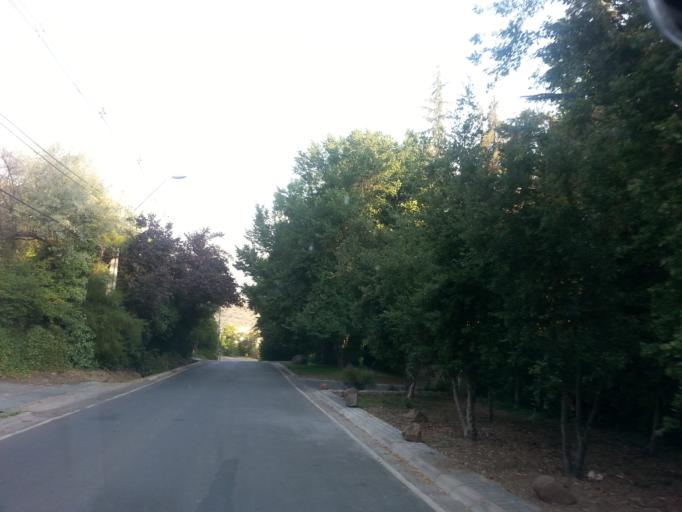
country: CL
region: Santiago Metropolitan
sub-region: Provincia de Santiago
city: Villa Presidente Frei, Nunoa, Santiago, Chile
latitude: -33.3622
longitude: -70.5586
